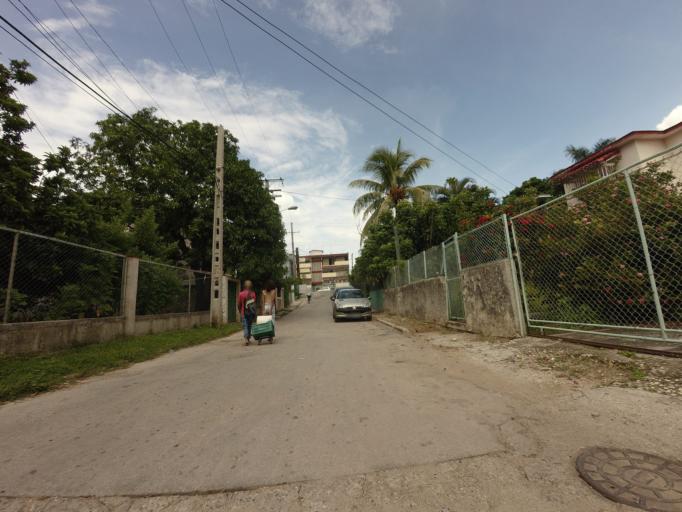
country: CU
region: La Habana
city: Cerro
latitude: 23.1026
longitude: -82.4406
